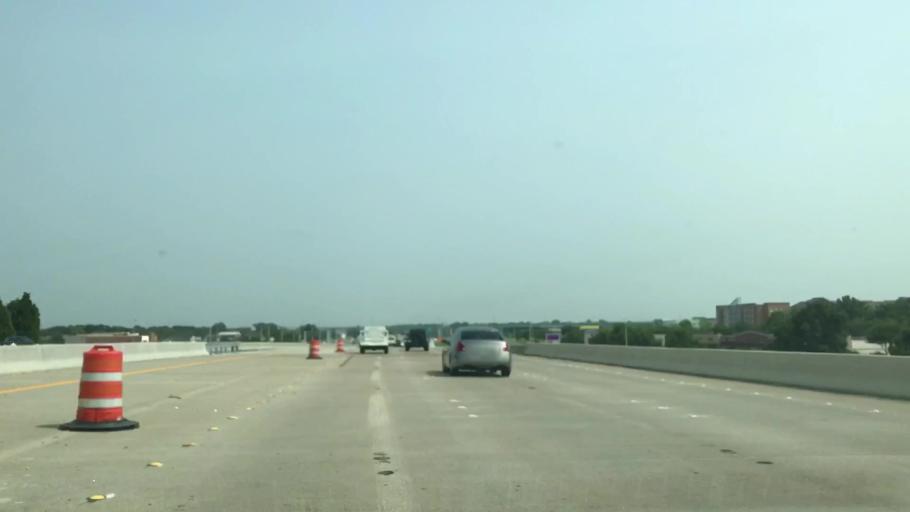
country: US
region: Texas
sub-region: Dallas County
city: Sachse
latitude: 32.9660
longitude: -96.6421
